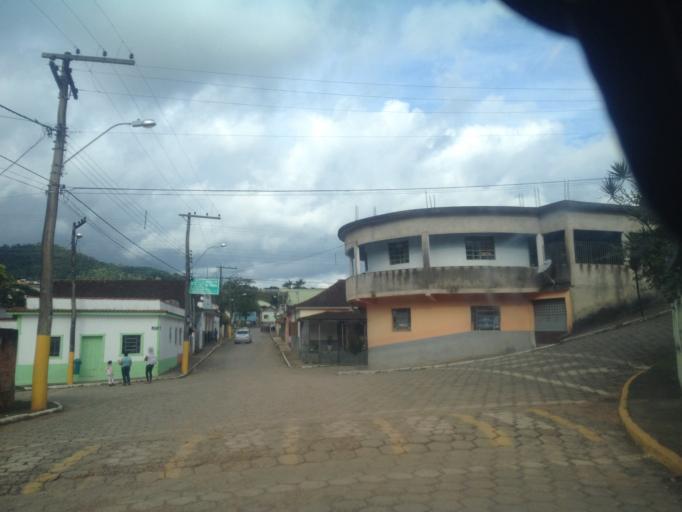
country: BR
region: Rio de Janeiro
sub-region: Quatis
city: Quatis
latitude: -22.2086
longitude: -44.2362
